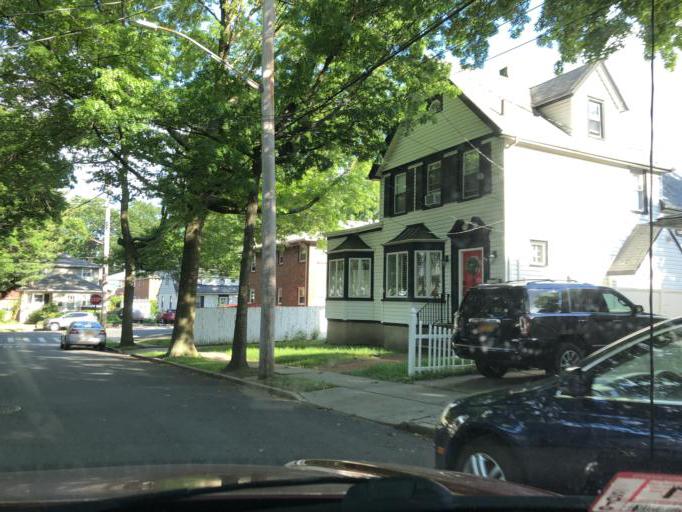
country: US
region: New York
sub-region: Richmond County
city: Staten Island
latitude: 40.5944
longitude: -74.0927
